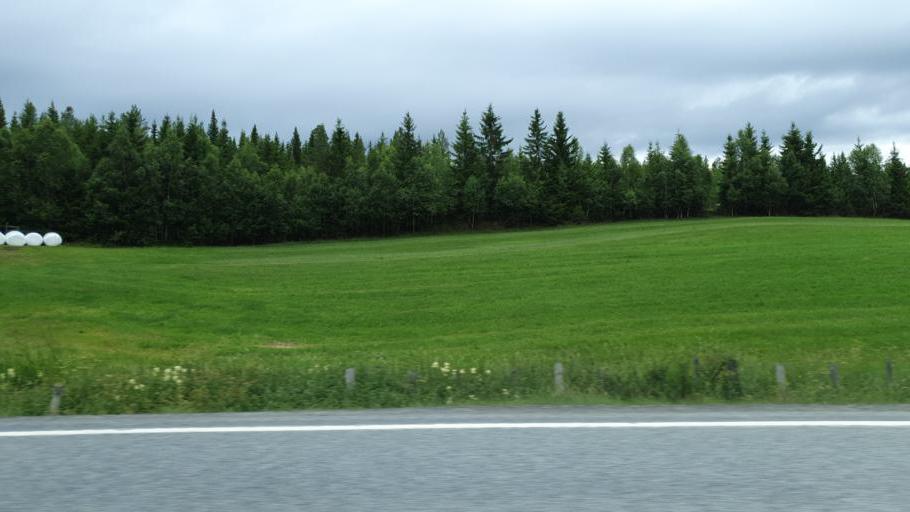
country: NO
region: Sor-Trondelag
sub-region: Rennebu
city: Berkak
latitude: 62.8853
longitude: 10.0999
